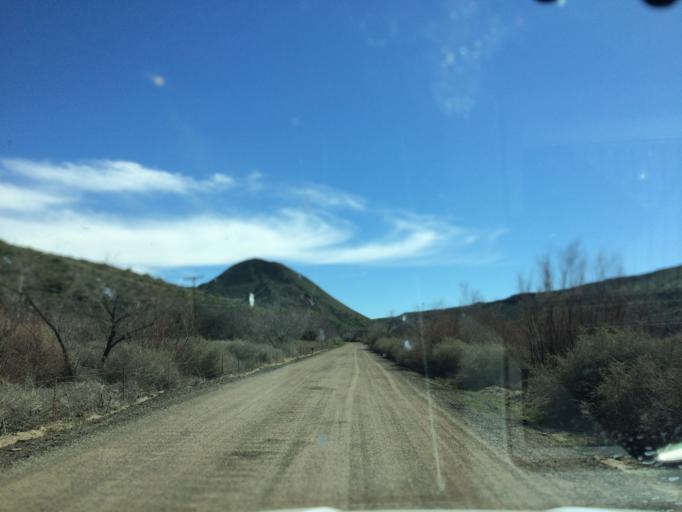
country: MX
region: Baja California
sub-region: Tecate
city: Cereso del Hongo
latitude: 32.6502
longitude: -116.1869
